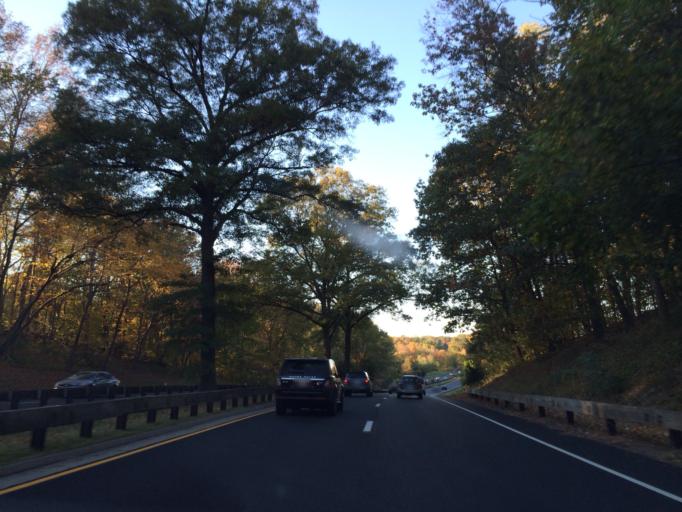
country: US
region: Connecticut
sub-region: Fairfield County
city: Glenville
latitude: 41.0540
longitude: -73.6739
